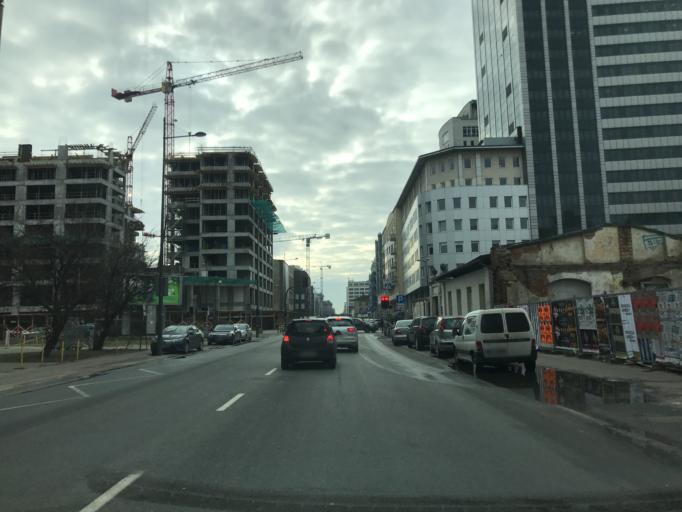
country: PL
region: Masovian Voivodeship
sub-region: Warszawa
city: Wola
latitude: 52.2354
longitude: 20.9902
